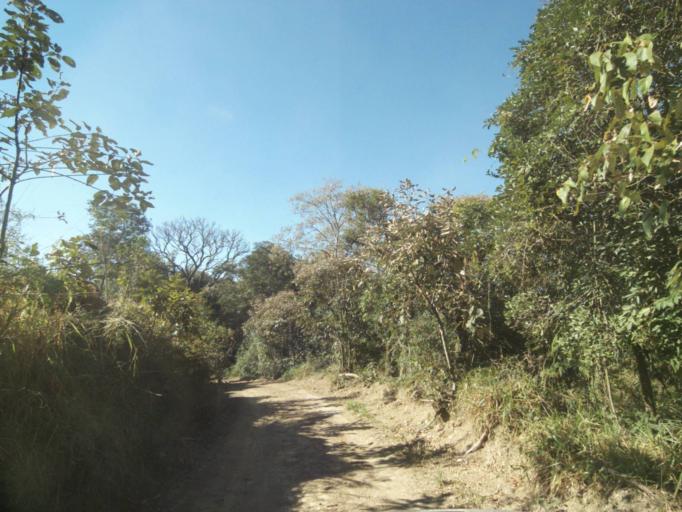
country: BR
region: Parana
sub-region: Tibagi
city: Tibagi
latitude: -24.5790
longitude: -50.4803
